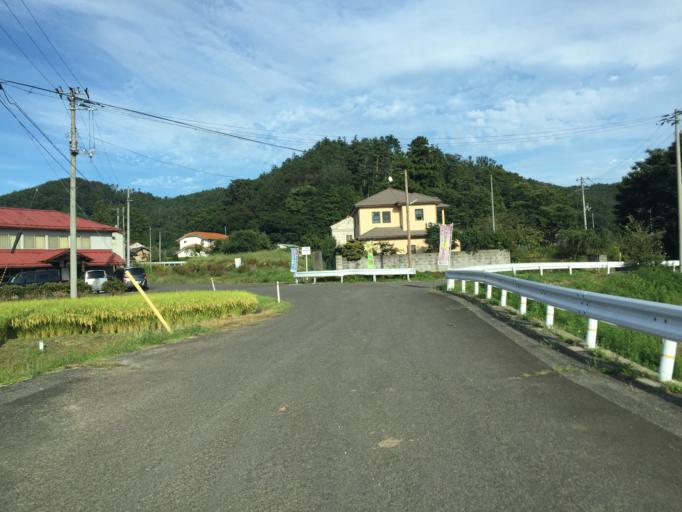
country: JP
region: Fukushima
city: Hobaramachi
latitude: 37.8904
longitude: 140.5342
